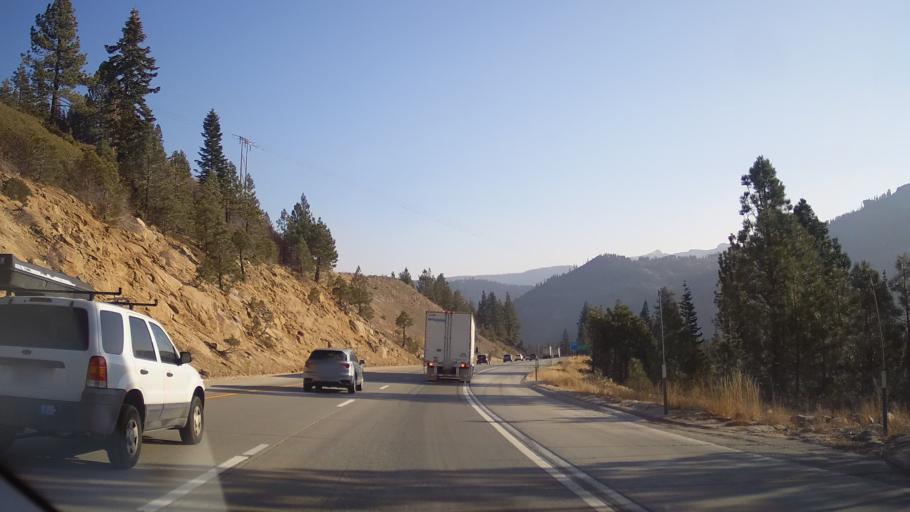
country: US
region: California
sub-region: Nevada County
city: Truckee
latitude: 39.3371
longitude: -120.3073
